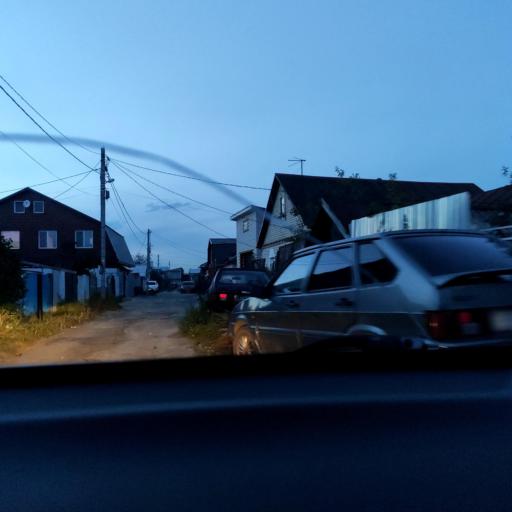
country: RU
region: Tatarstan
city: Staroye Arakchino
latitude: 55.8764
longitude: 49.0453
